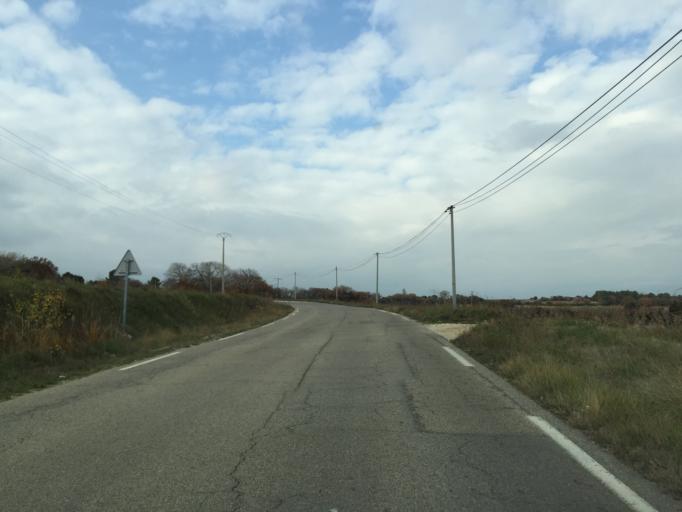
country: FR
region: Provence-Alpes-Cote d'Azur
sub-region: Departement du Vaucluse
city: Bedarrides
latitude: 44.0474
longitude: 4.8800
